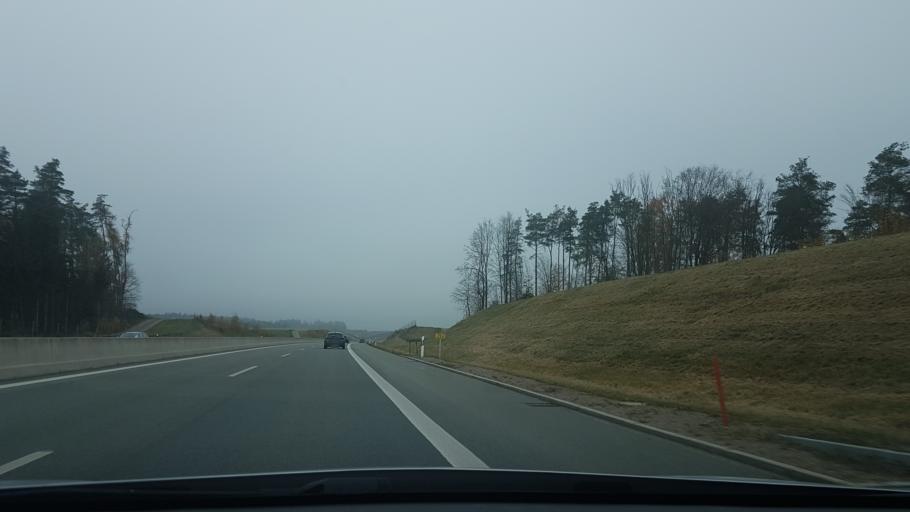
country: DE
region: Bavaria
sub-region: Lower Bavaria
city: Ergoldsbach
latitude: 48.6950
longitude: 12.1798
